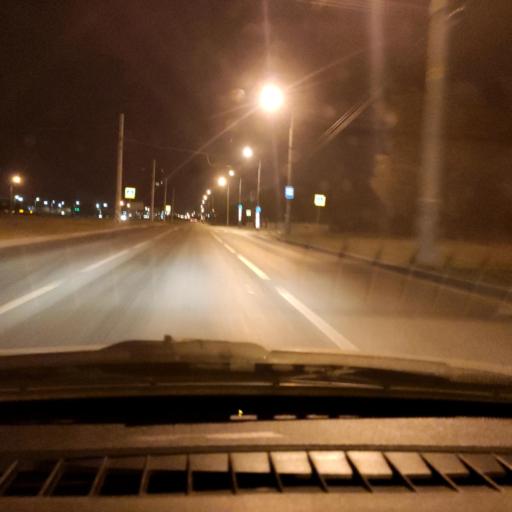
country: RU
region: Samara
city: Tol'yatti
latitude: 53.5564
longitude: 49.2487
